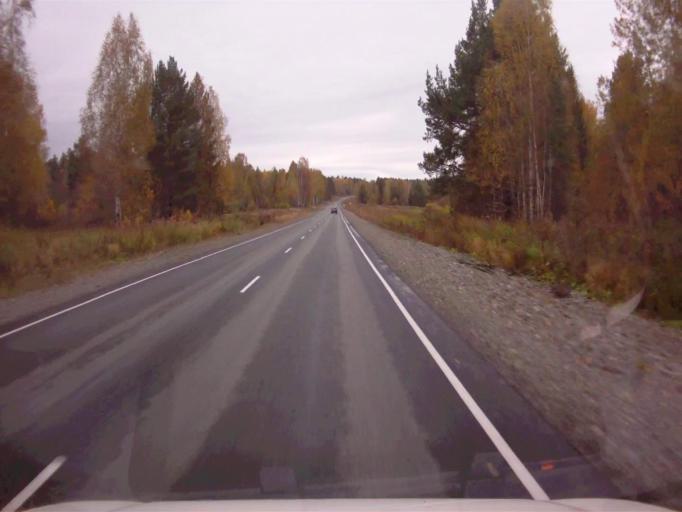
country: RU
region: Chelyabinsk
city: Nyazepetrovsk
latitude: 56.0449
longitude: 59.7617
